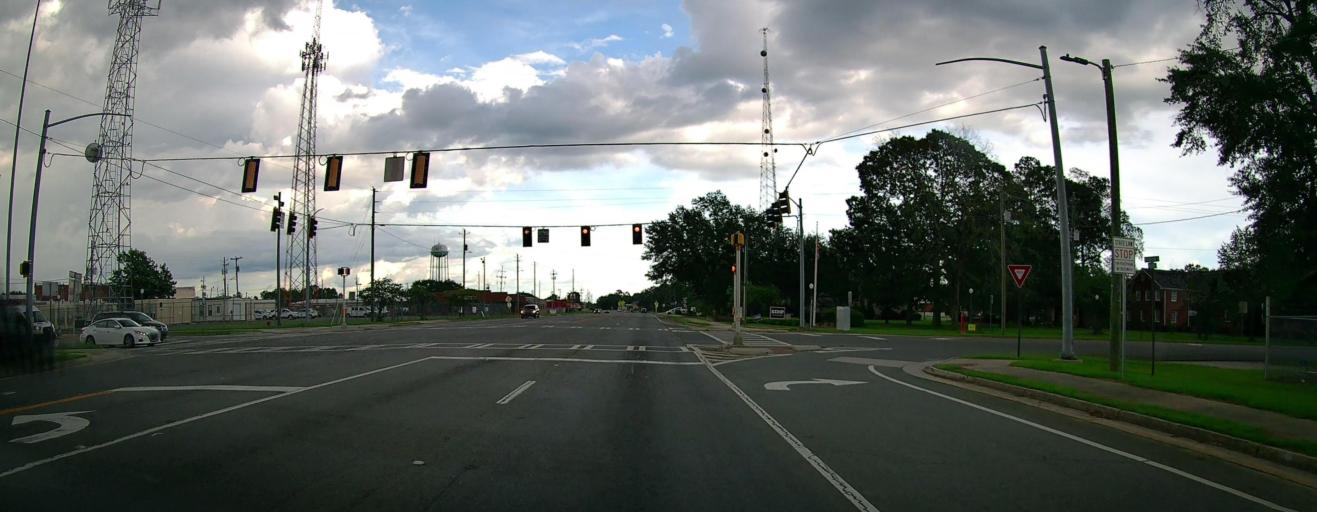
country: US
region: Georgia
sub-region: Taylor County
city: Reynolds
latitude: 32.5583
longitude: -84.0968
